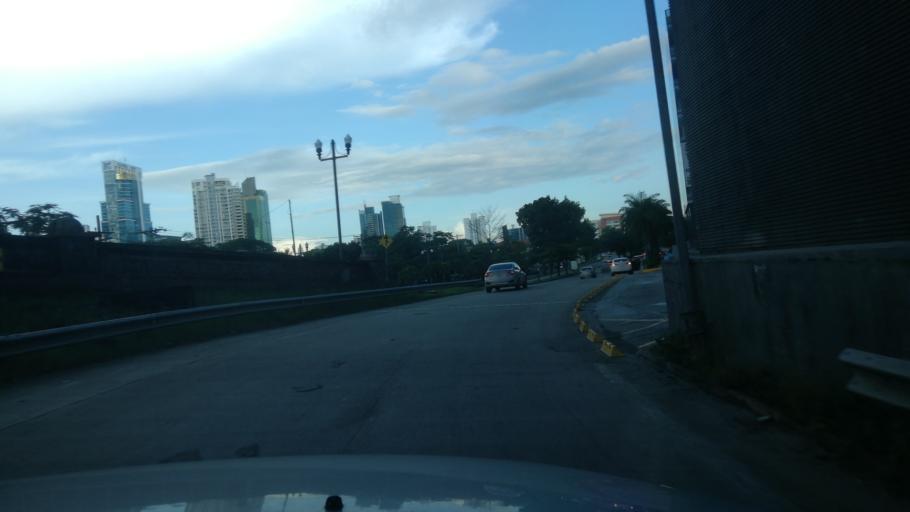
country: PA
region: Panama
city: Panama
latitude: 8.9800
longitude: -79.5101
